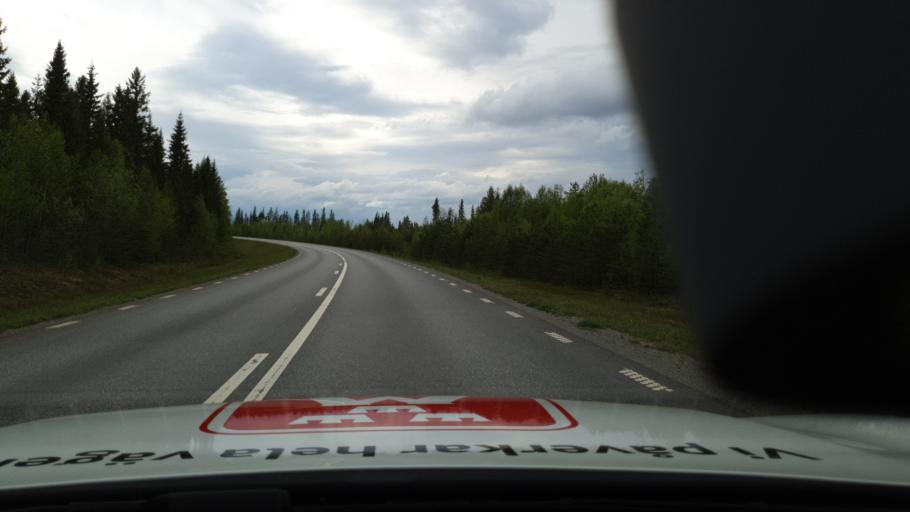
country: SE
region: Vaesterbotten
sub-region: Dorotea Kommun
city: Dorotea
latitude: 64.3423
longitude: 16.6463
